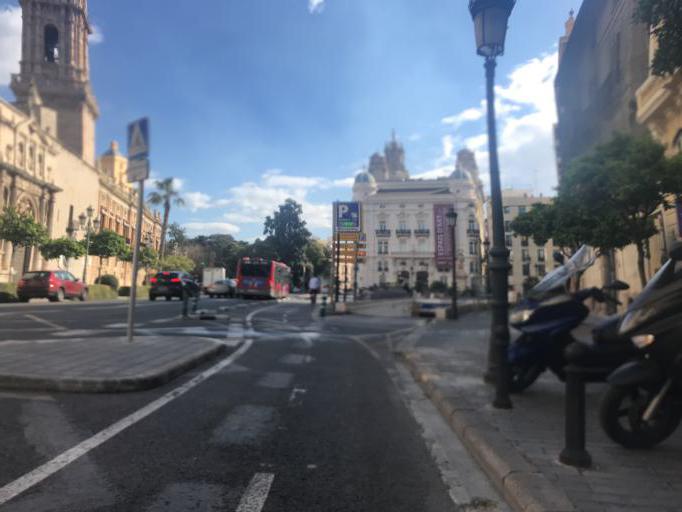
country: ES
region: Valencia
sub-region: Provincia de Valencia
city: Valencia
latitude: 39.4750
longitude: -0.3698
